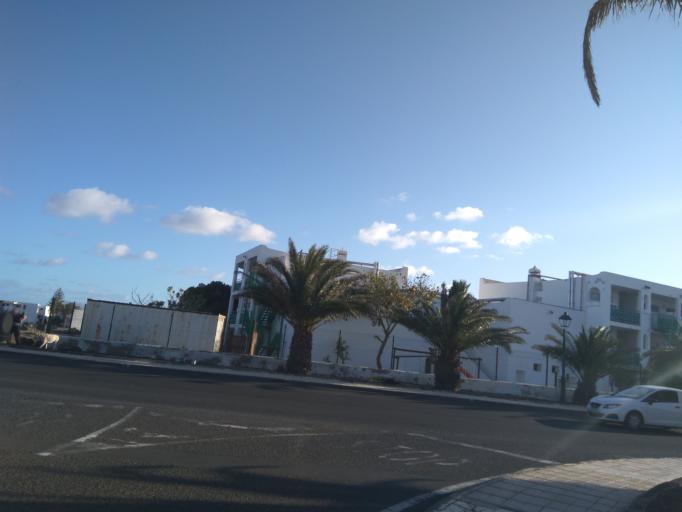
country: ES
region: Canary Islands
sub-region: Provincia de Las Palmas
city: Arrecife
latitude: 29.0052
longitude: -13.4906
